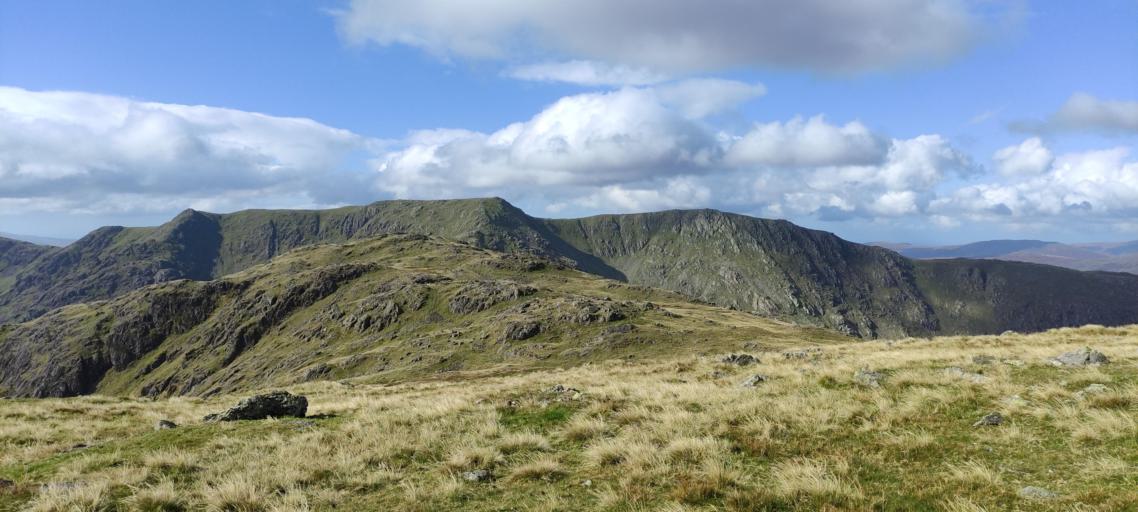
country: GB
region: England
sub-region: Cumbria
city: Ambleside
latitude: 54.3992
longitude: -3.0979
